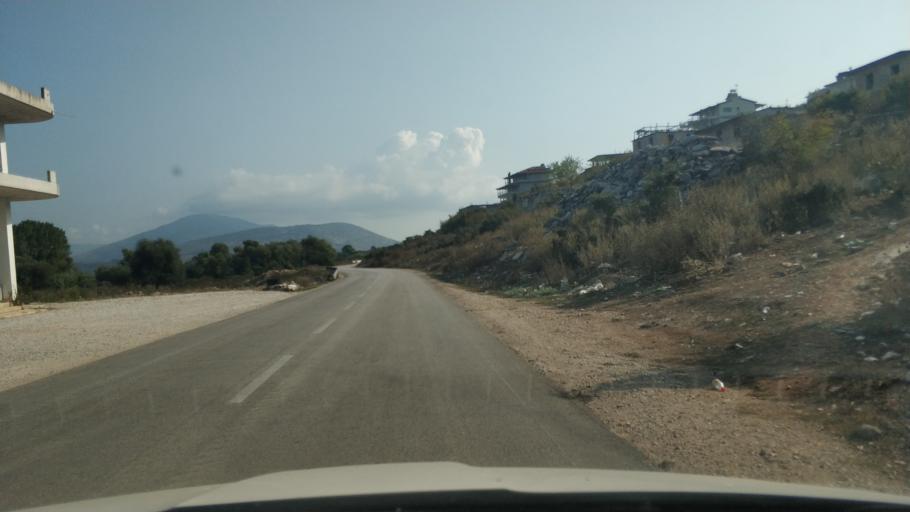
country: AL
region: Vlore
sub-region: Rrethi i Sarandes
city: Sarande
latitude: 39.8488
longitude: 20.0358
